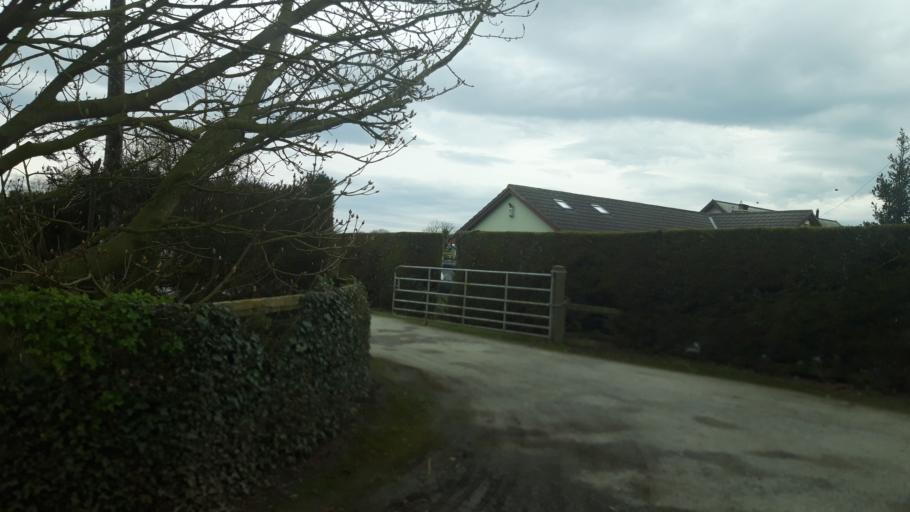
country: IE
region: Leinster
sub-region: Kildare
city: Celbridge
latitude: 53.3546
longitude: -6.5539
